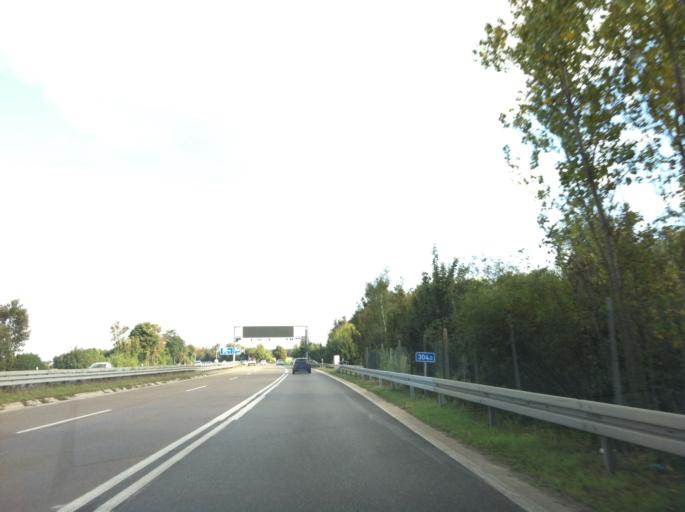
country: DE
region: Hesse
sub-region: Regierungsbezirk Darmstadt
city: Bad Homburg vor der Hoehe
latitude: 50.2059
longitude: 8.6246
